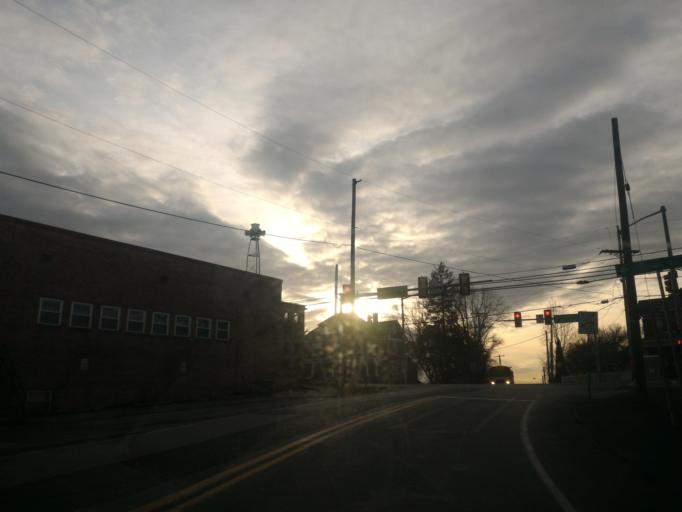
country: US
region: Pennsylvania
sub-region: York County
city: Jacobus
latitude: 39.8800
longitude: -76.7094
